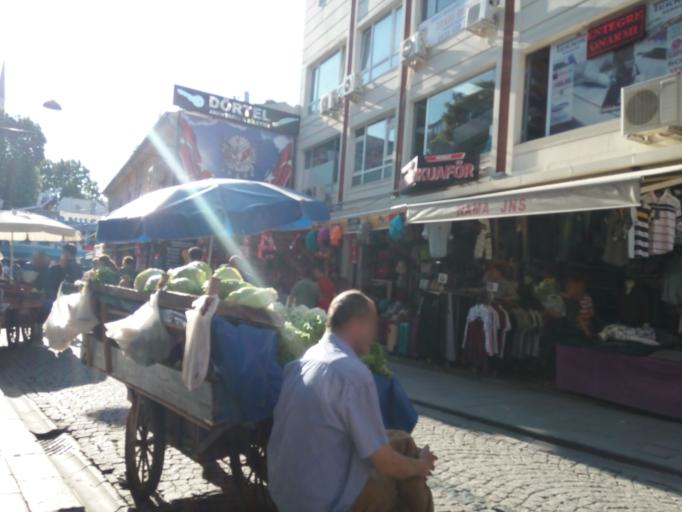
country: TR
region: Istanbul
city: UEskuedar
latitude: 41.0248
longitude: 29.0170
